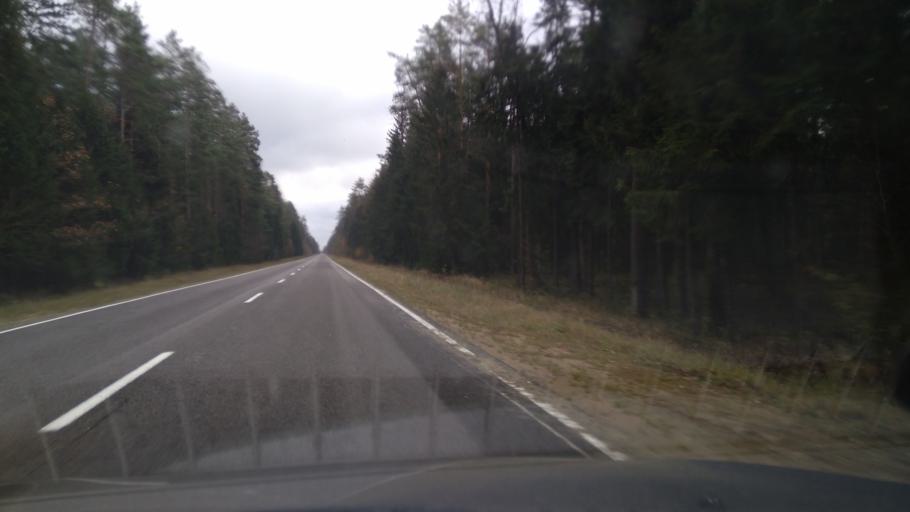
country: BY
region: Minsk
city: Urechcha
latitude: 53.2146
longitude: 27.8631
